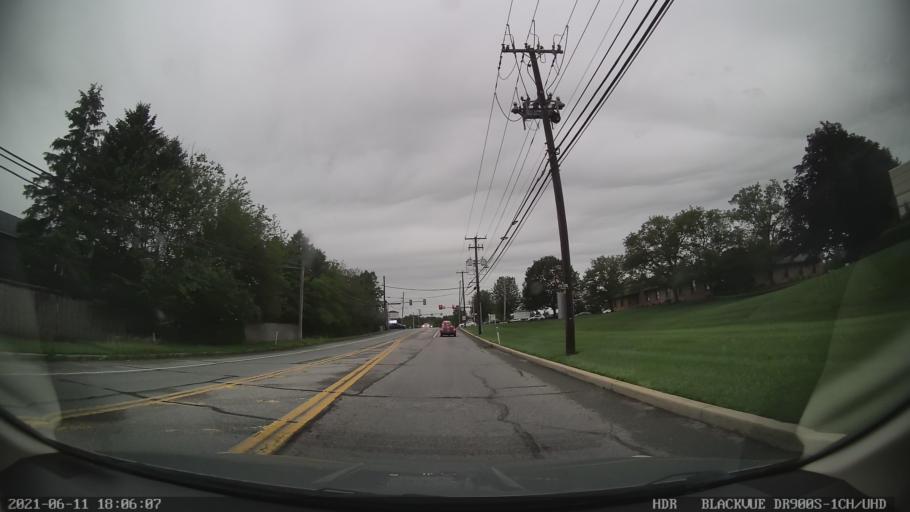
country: US
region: Pennsylvania
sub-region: Berks County
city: Spring Ridge
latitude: 40.3419
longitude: -75.9904
